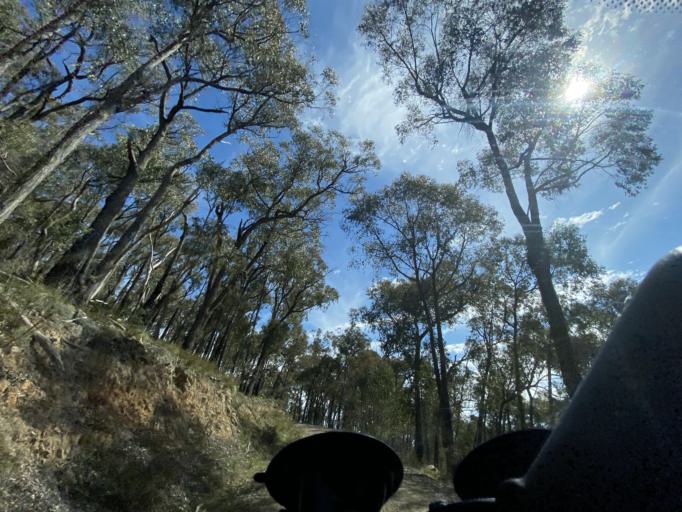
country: AU
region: Victoria
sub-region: Mansfield
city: Mansfield
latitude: -36.8037
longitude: 146.1086
